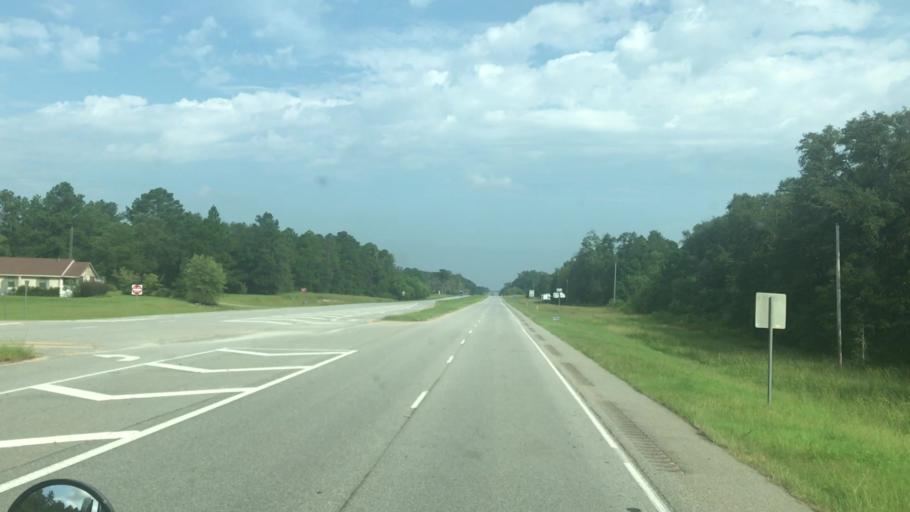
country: US
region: Georgia
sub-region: Early County
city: Blakely
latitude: 31.2887
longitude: -84.8466
